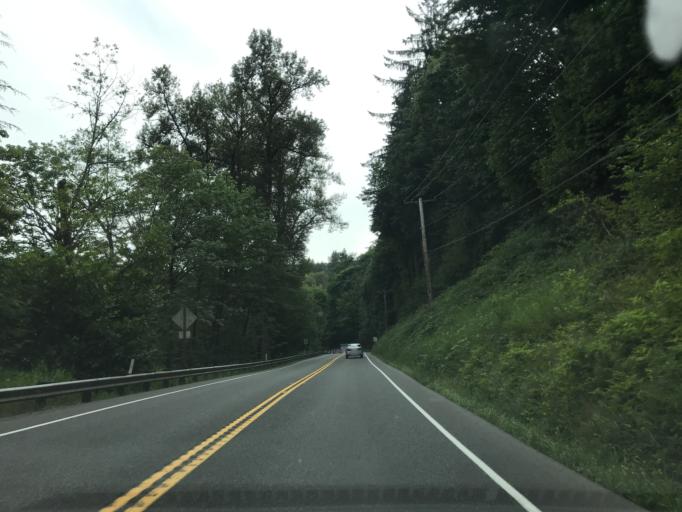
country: US
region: Washington
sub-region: King County
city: Fall City
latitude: 47.5277
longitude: -121.9245
